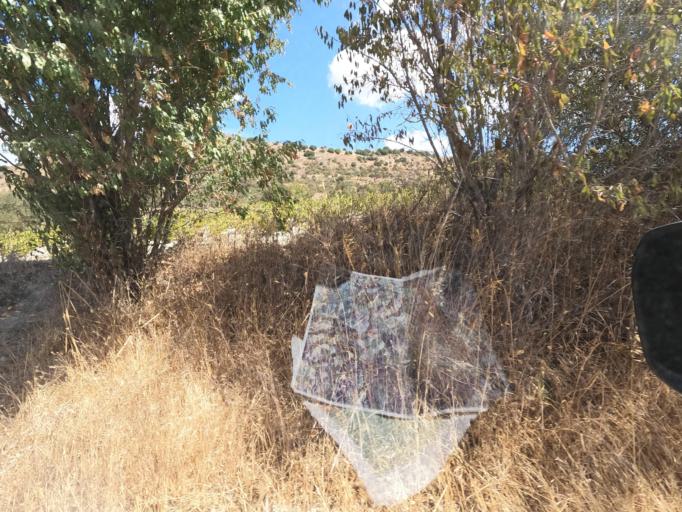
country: CY
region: Pafos
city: Mesogi
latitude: 34.8286
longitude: 32.5472
